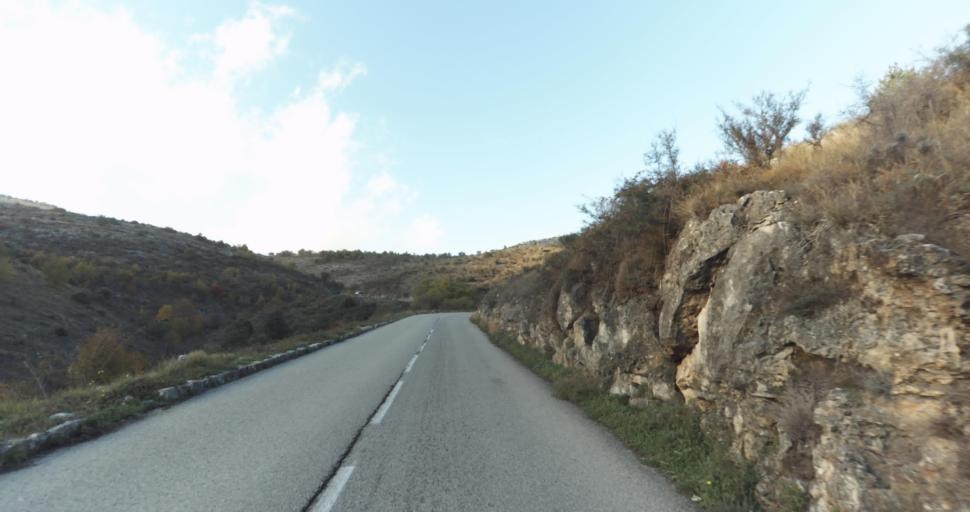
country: FR
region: Provence-Alpes-Cote d'Azur
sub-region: Departement des Alpes-Maritimes
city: Vence
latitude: 43.7507
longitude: 7.0960
